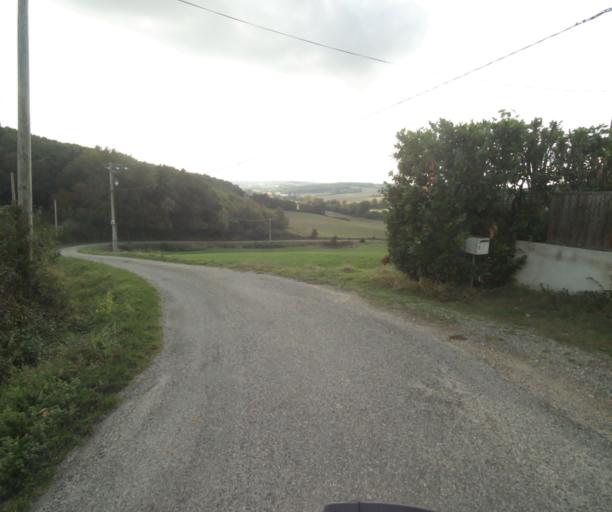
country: FR
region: Midi-Pyrenees
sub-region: Departement de la Haute-Garonne
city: Launac
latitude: 43.8074
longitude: 1.1207
